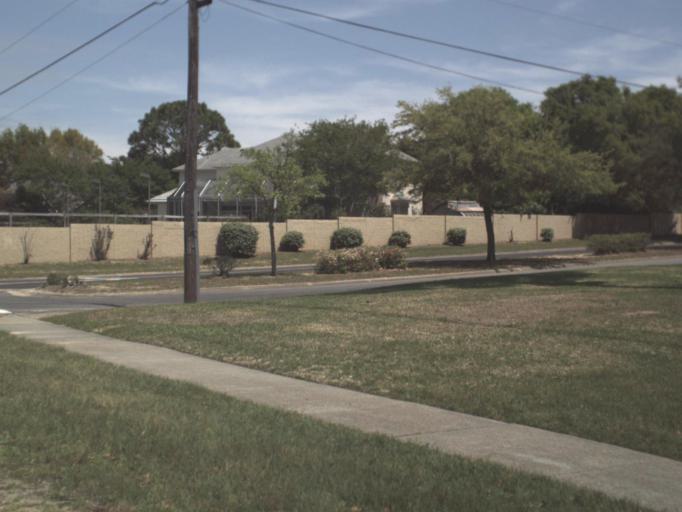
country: US
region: Florida
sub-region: Escambia County
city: East Pensacola Heights
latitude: 30.4397
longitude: -87.1821
